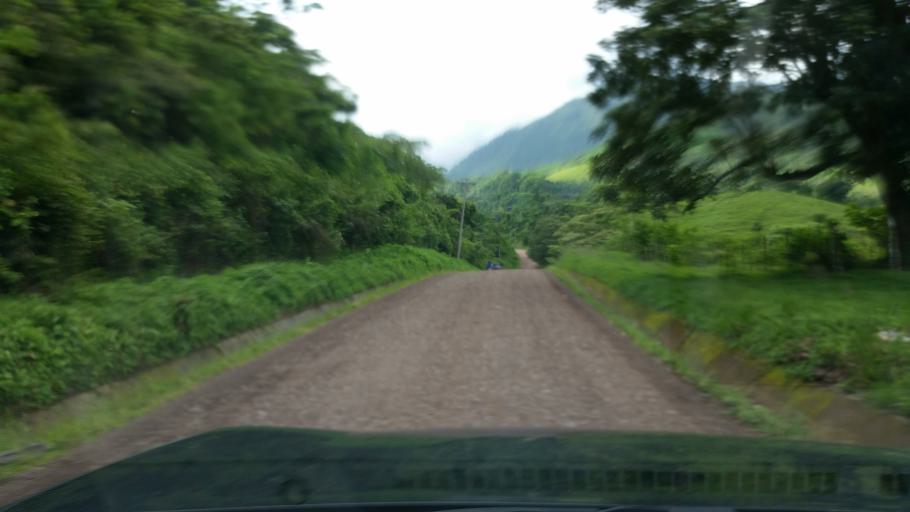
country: NI
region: Jinotega
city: Jinotega
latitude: 13.2264
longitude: -85.7300
